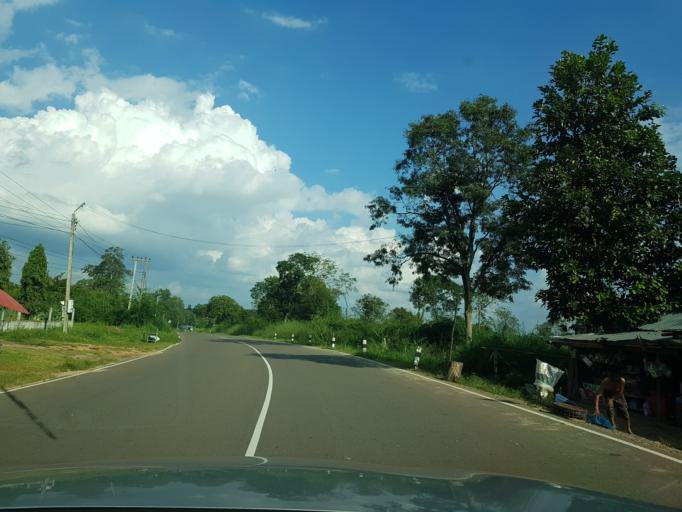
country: TH
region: Nong Khai
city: Pho Tak
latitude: 17.9876
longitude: 102.4322
